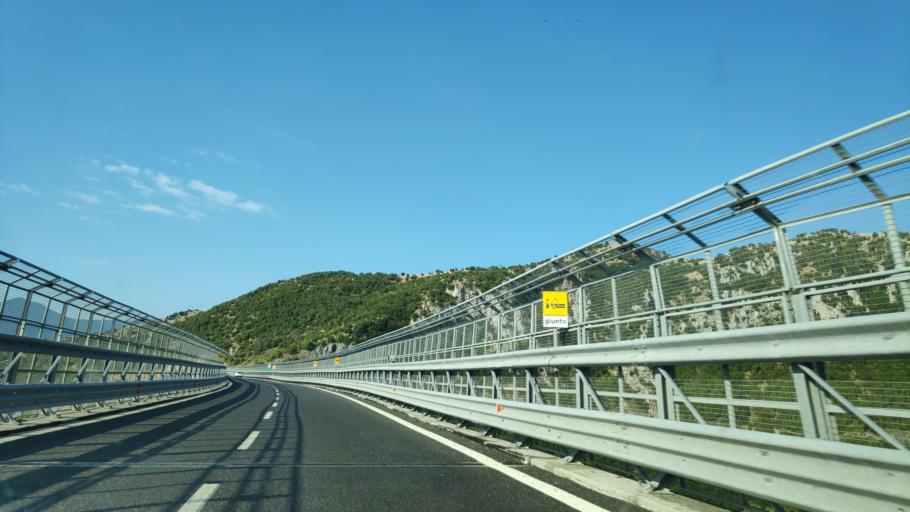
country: IT
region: Calabria
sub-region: Provincia di Cosenza
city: Morano Calabro
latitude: 39.8808
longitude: 16.1301
